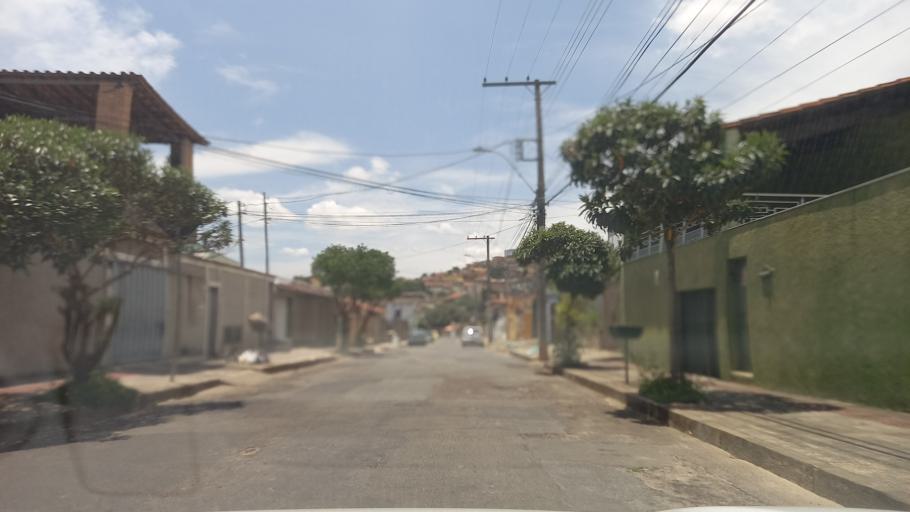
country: BR
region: Minas Gerais
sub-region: Contagem
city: Contagem
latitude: -19.9056
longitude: -44.0075
